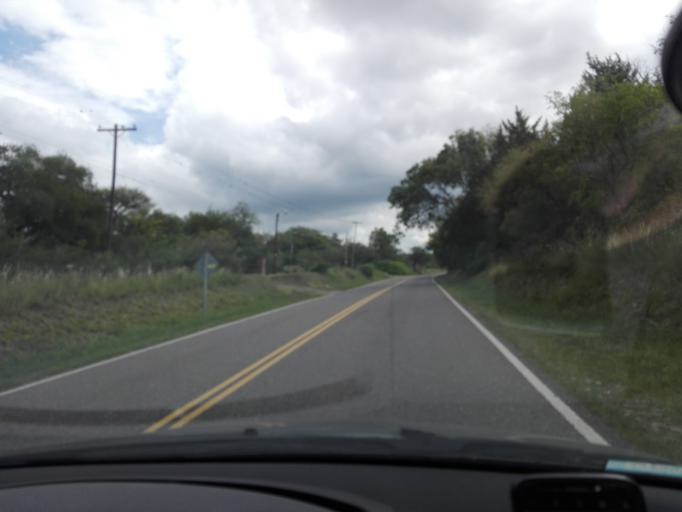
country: AR
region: Cordoba
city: Alta Gracia
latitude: -31.5877
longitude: -64.4652
